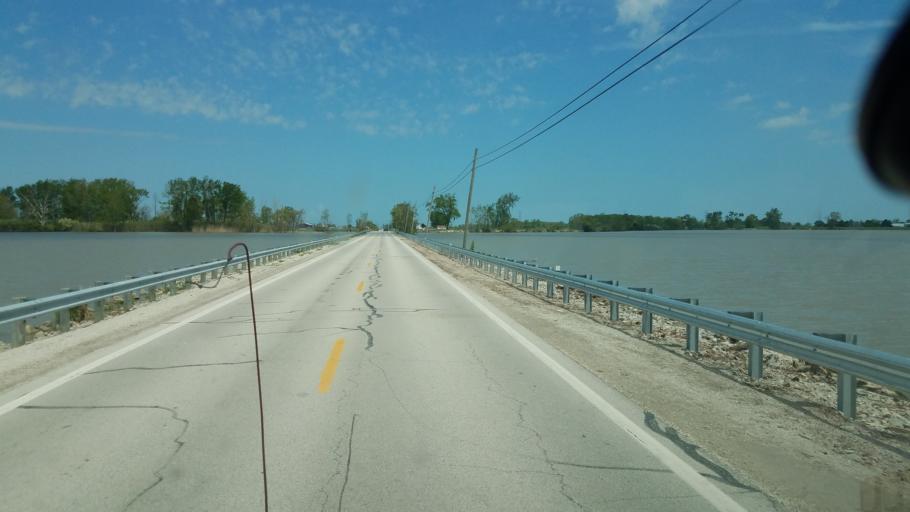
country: US
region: Ohio
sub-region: Ottawa County
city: Oak Harbor
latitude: 41.5762
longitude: -83.1449
